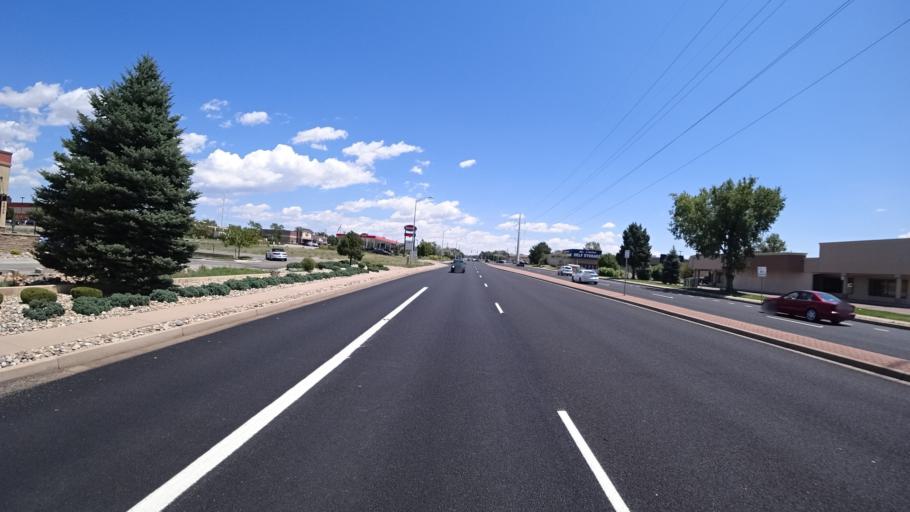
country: US
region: Colorado
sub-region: El Paso County
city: Stratmoor
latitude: 38.7891
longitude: -104.7567
